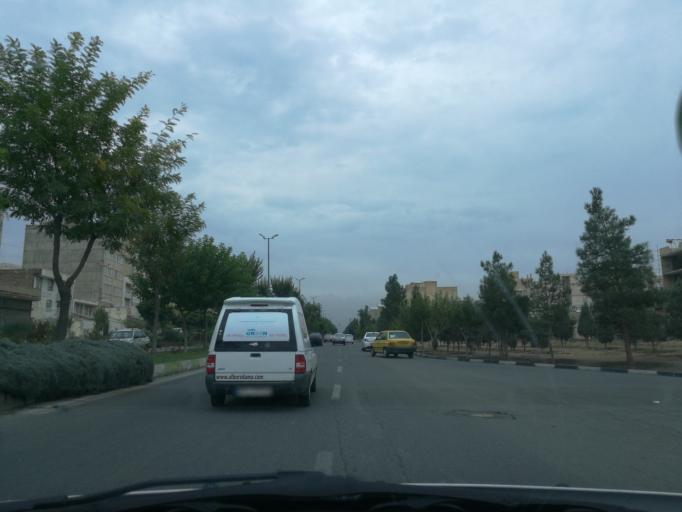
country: IR
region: Alborz
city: Karaj
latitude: 35.8612
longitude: 50.9387
